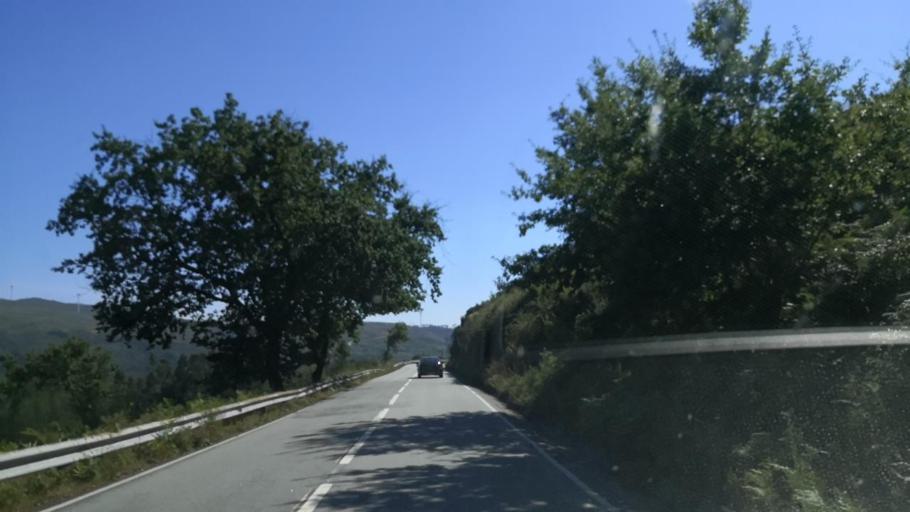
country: PT
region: Braga
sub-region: Fafe
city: Fafe
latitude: 41.4968
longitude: -8.0880
